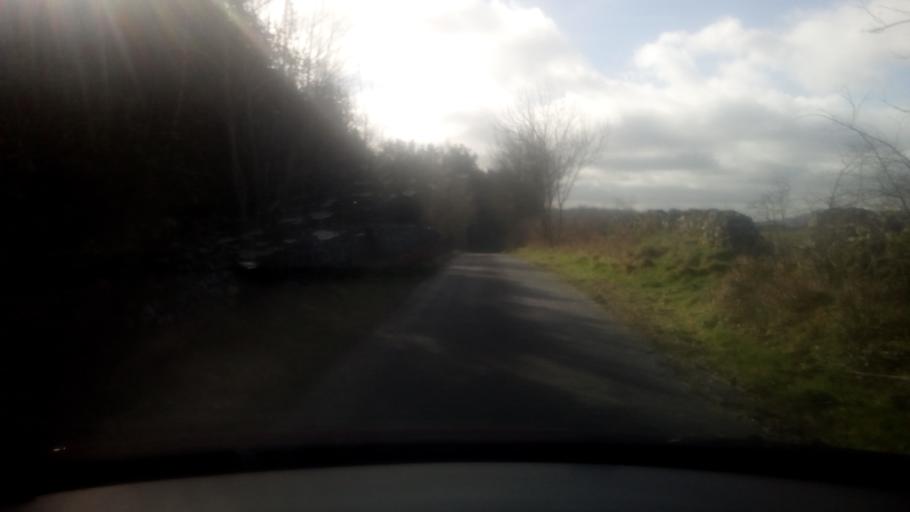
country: GB
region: Scotland
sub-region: The Scottish Borders
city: Jedburgh
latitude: 55.5260
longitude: -2.5745
